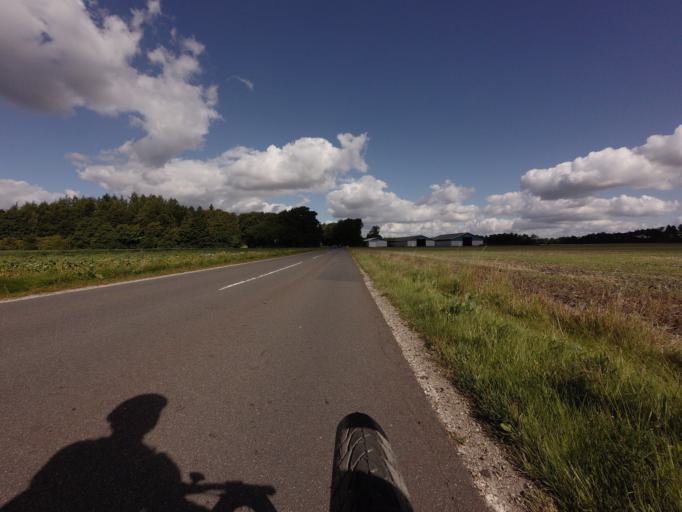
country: DK
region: Central Jutland
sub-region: Ikast-Brande Kommune
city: Brande
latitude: 55.9796
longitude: 9.1436
